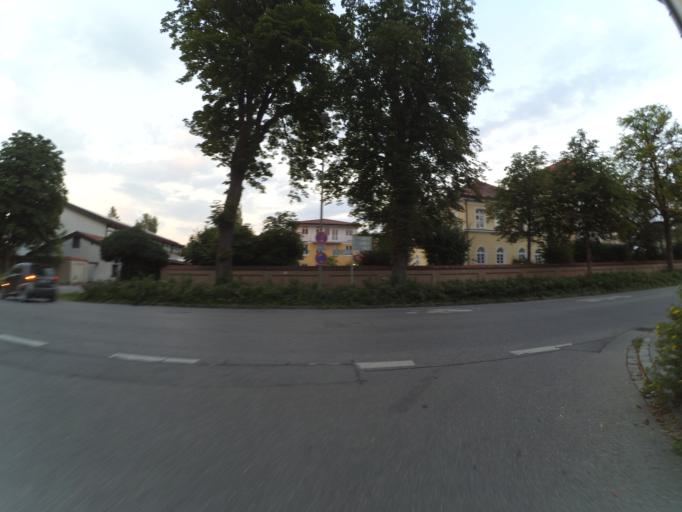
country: DE
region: Bavaria
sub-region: Swabia
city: Turkheim
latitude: 48.0586
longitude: 10.6396
